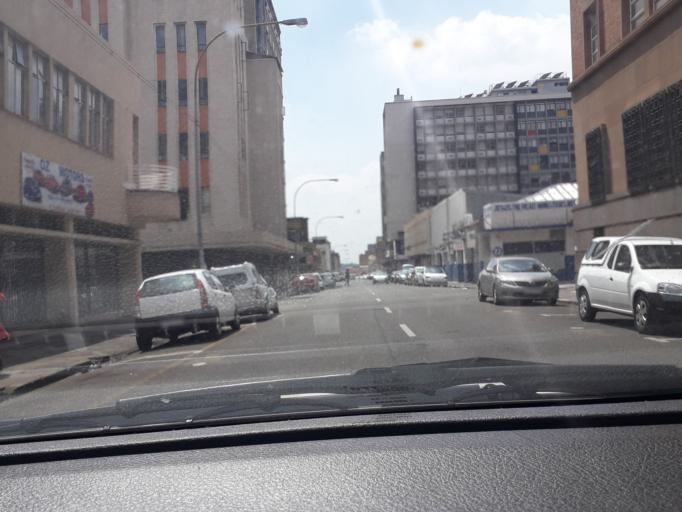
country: ZA
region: Gauteng
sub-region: City of Johannesburg Metropolitan Municipality
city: Johannesburg
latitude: -26.2083
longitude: 28.0432
